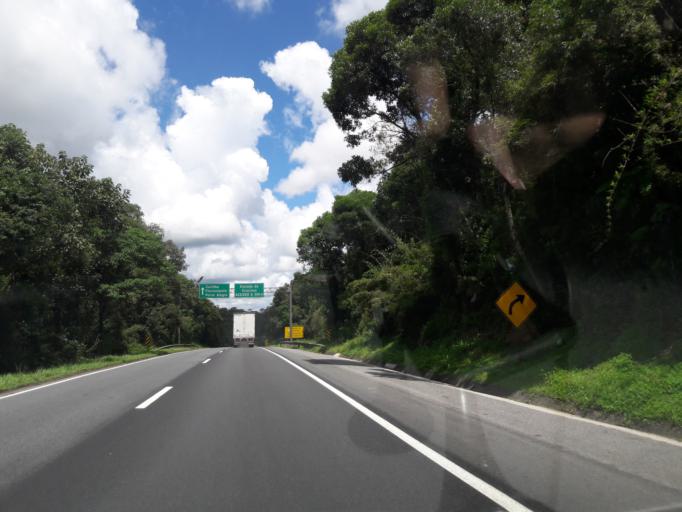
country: BR
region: Parana
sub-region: Campina Grande Do Sul
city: Campina Grande do Sul
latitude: -25.3007
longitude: -48.9423
